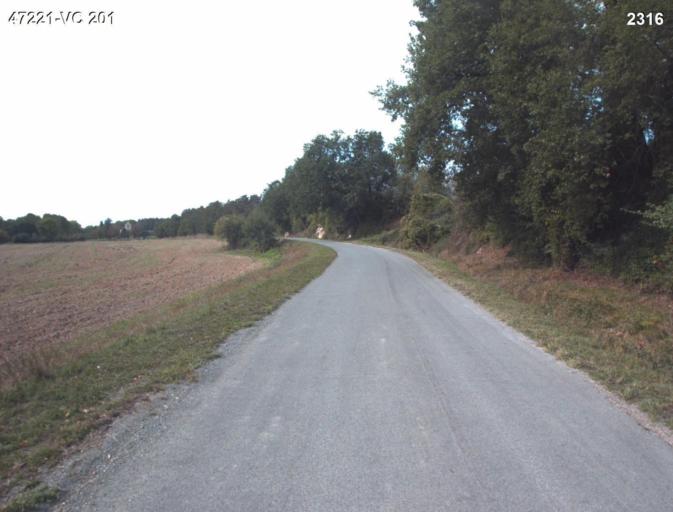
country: FR
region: Aquitaine
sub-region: Departement du Lot-et-Garonne
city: Mezin
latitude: 44.1093
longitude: 0.2464
